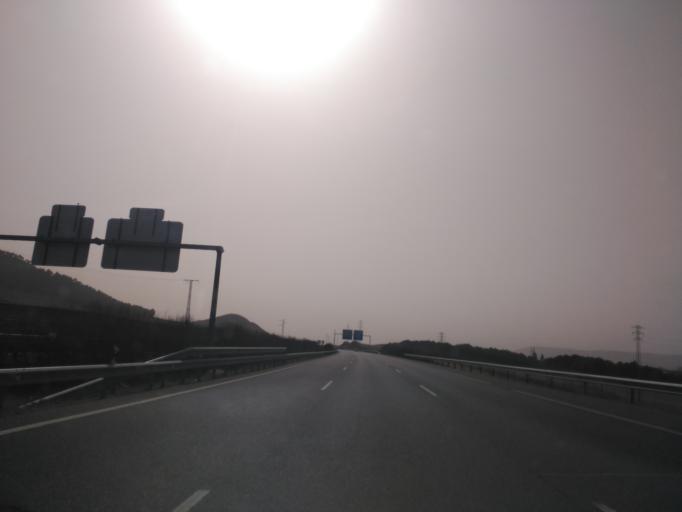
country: ES
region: Castille and Leon
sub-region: Provincia de Palencia
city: Palencia
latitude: 41.9954
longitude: -4.5029
